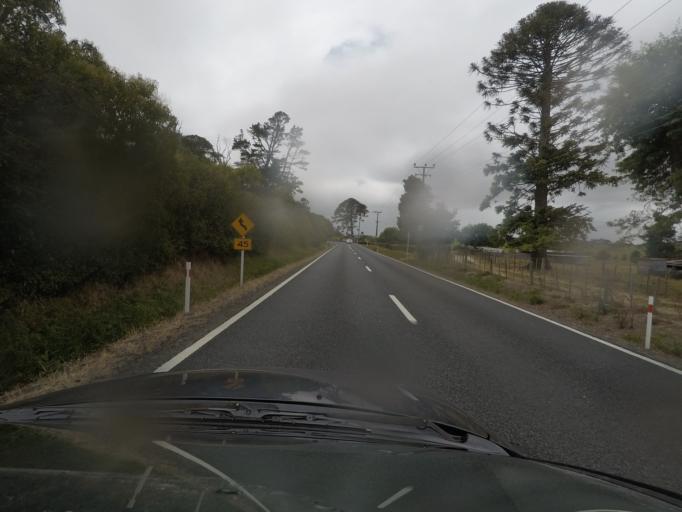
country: NZ
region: Auckland
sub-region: Auckland
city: Warkworth
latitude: -36.3424
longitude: 174.7045
